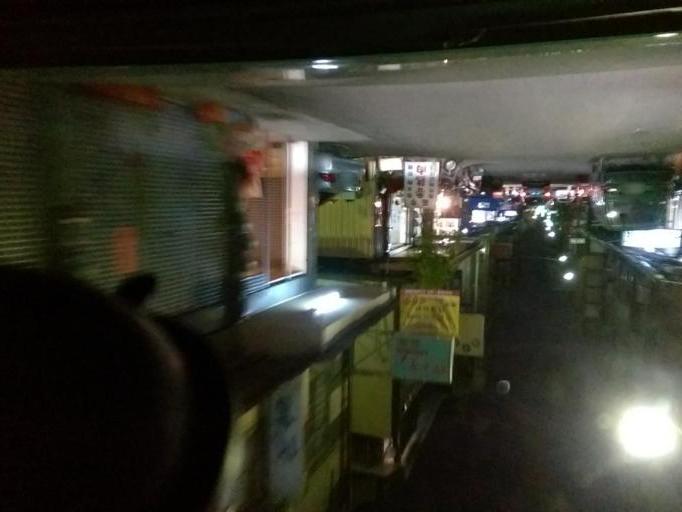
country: TW
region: Taiwan
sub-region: Chiayi
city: Jiayi Shi
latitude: 23.4768
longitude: 120.4477
